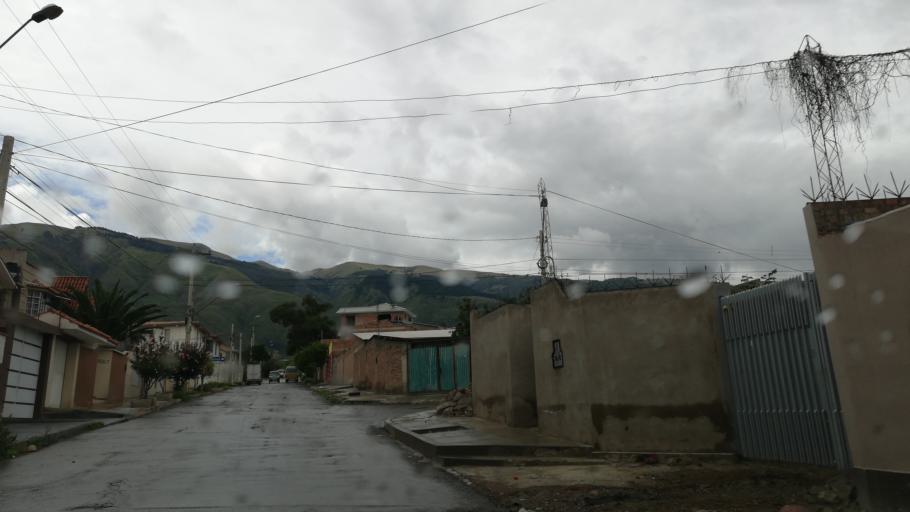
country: BO
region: Cochabamba
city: Cochabamba
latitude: -17.3528
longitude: -66.1764
